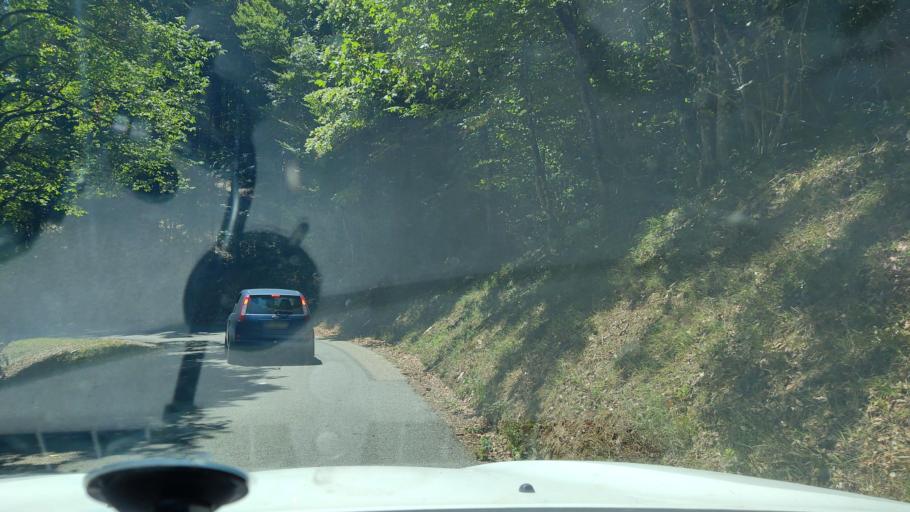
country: FR
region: Rhone-Alpes
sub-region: Departement de la Savoie
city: Le Bourget-du-Lac
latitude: 45.6566
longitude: 5.8354
